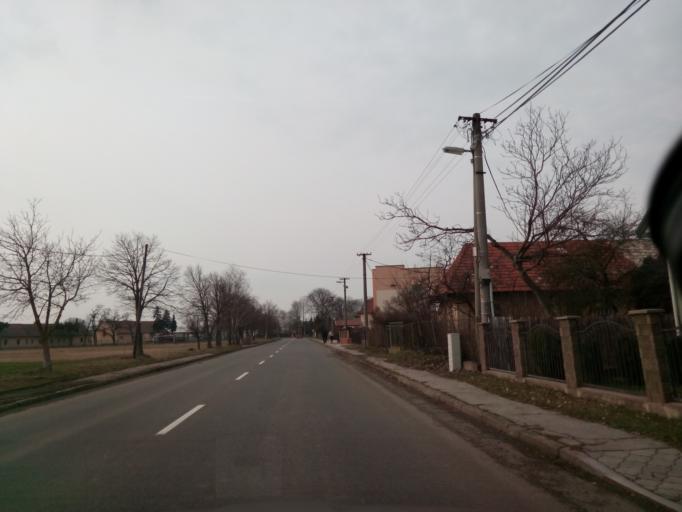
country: SK
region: Kosicky
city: Trebisov
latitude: 48.5556
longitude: 21.6765
